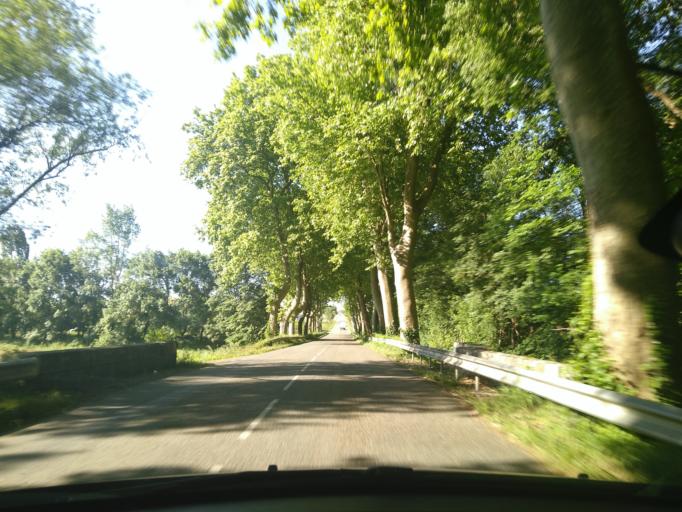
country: FR
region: Midi-Pyrenees
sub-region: Departement du Gers
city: Aubiet
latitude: 43.5311
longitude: 0.7651
